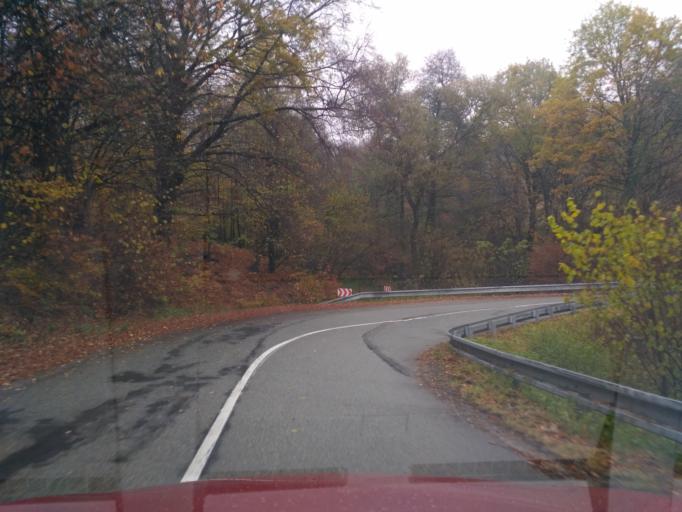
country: SK
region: Kosicky
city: Medzev
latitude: 48.7123
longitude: 20.7979
